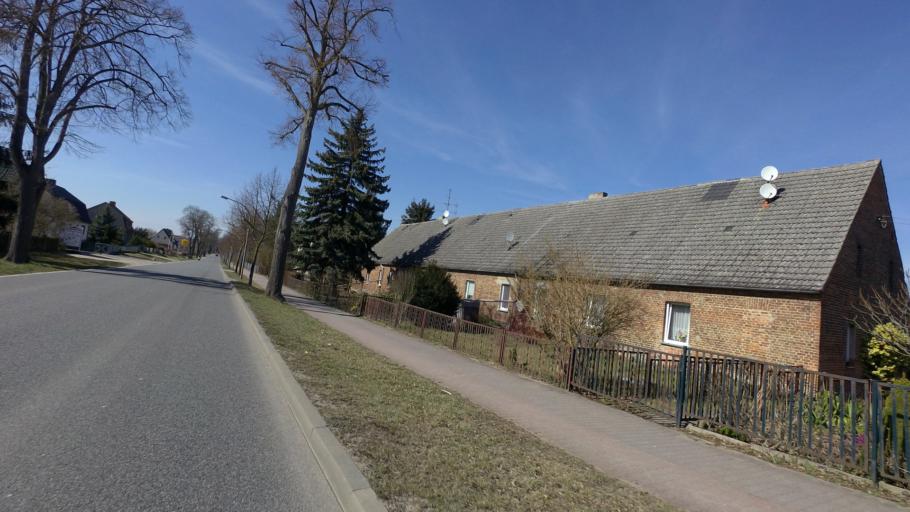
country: DE
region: Brandenburg
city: Muncheberg
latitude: 52.5095
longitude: 14.1265
